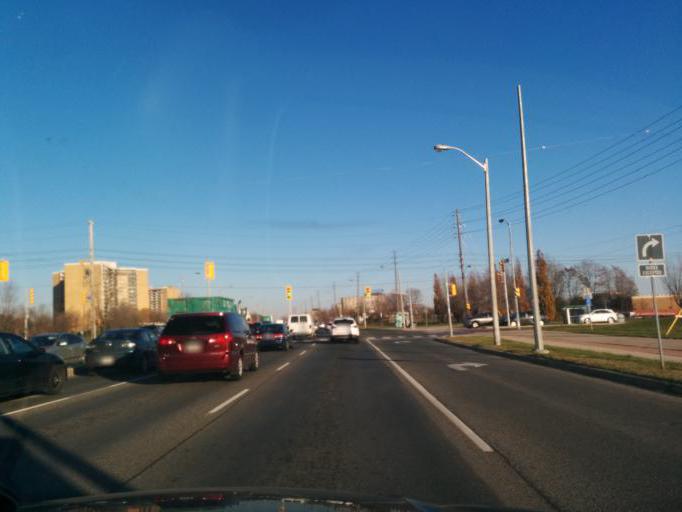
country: CA
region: Ontario
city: Etobicoke
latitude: 43.6743
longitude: -79.5639
